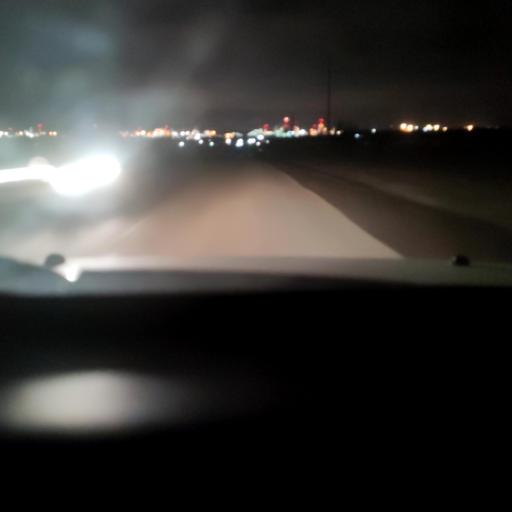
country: RU
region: Perm
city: Gamovo
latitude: 57.8846
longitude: 56.1041
